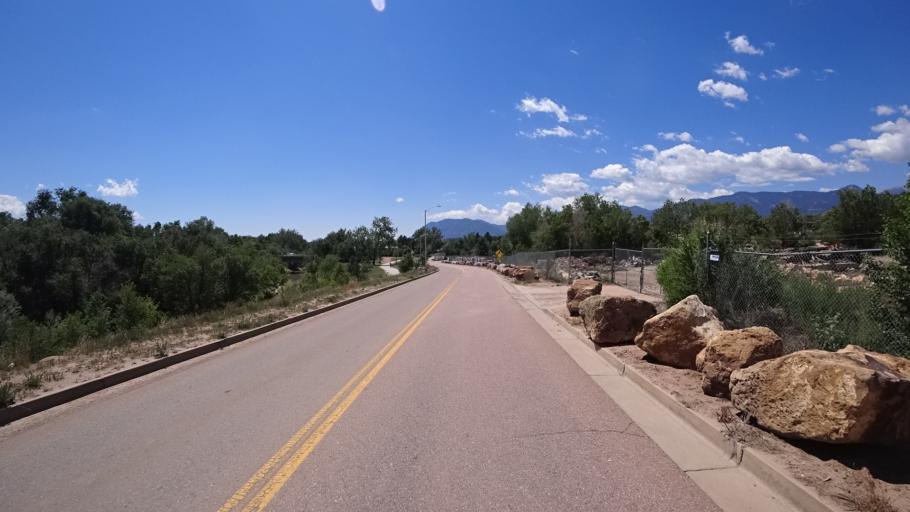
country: US
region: Colorado
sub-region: El Paso County
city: Colorado Springs
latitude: 38.8742
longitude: -104.8316
